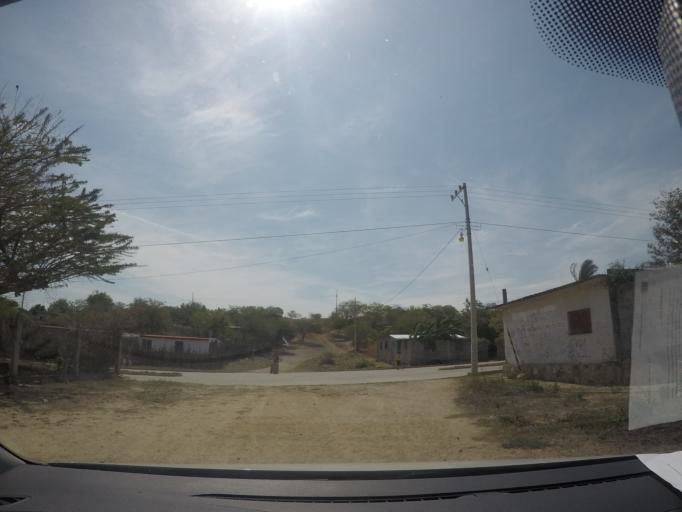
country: MX
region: Oaxaca
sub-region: Salina Cruz
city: Salina Cruz
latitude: 16.2188
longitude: -95.1264
